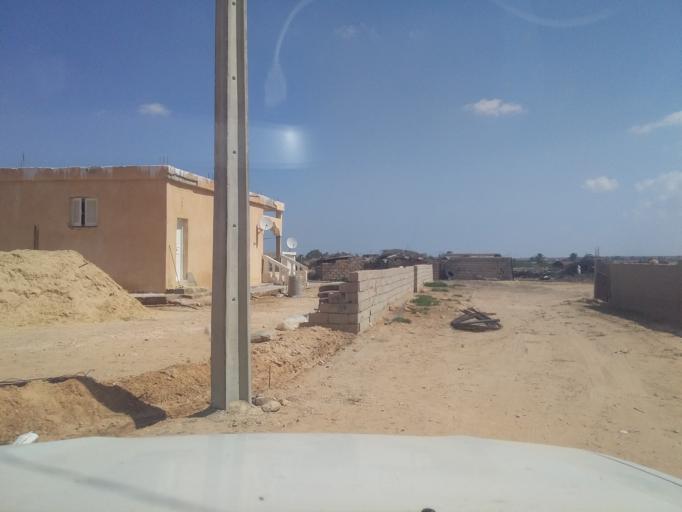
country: TN
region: Madanin
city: Medenine
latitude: 33.6113
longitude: 10.3125
